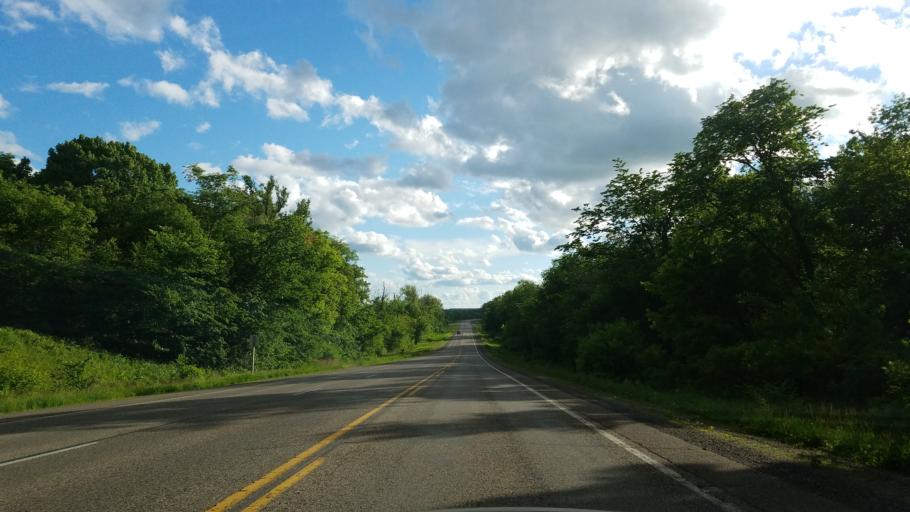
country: US
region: Wisconsin
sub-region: Polk County
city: Osceola
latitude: 45.3400
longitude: -92.6749
